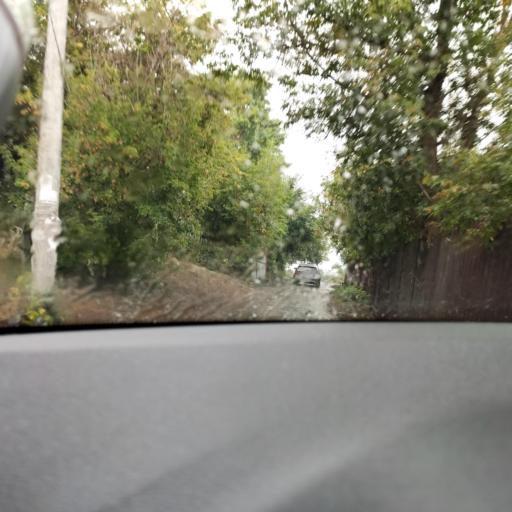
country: RU
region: Samara
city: Samara
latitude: 53.1751
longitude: 50.1538
